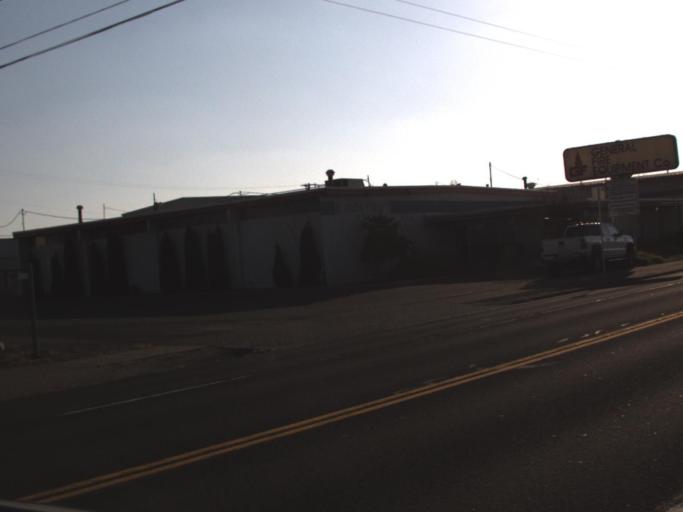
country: US
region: Washington
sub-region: Spokane County
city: Millwood
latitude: 47.6709
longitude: -117.3509
